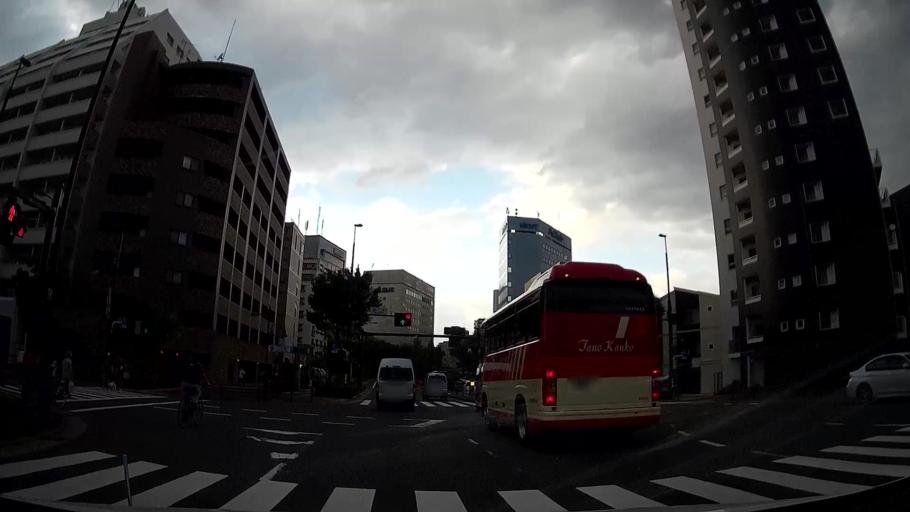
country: JP
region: Tokyo
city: Tokyo
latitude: 35.7009
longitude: 139.6829
